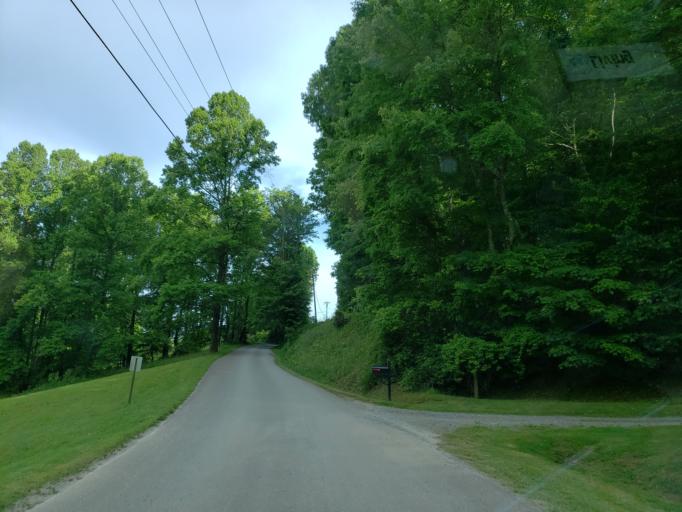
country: US
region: Georgia
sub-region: Fannin County
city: Blue Ridge
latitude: 34.8357
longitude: -84.4114
